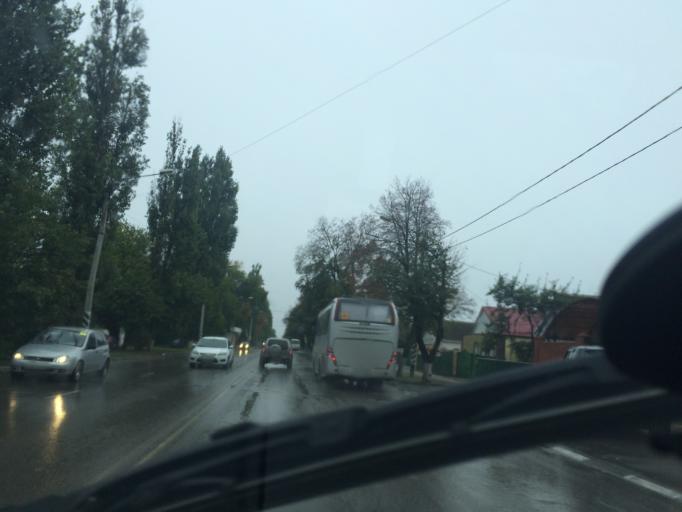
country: RU
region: Rostov
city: Azov
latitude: 47.0985
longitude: 39.4424
